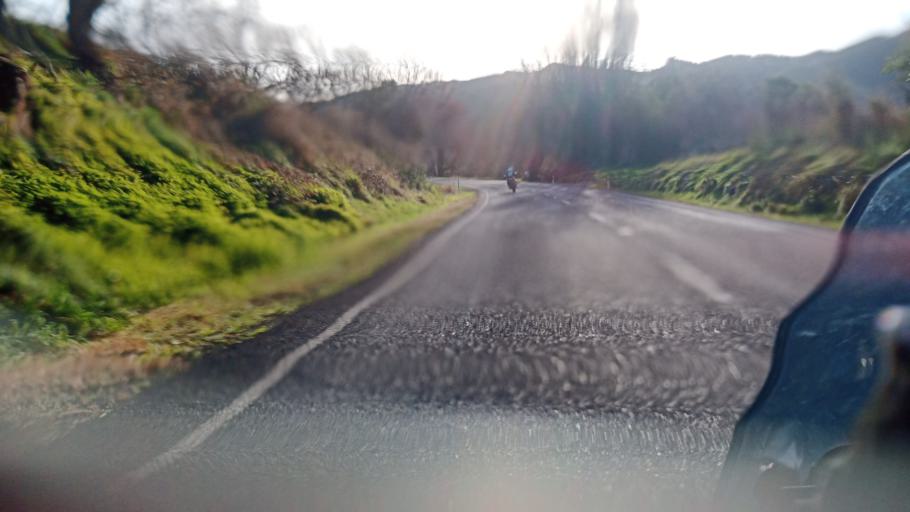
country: NZ
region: Gisborne
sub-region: Gisborne District
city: Gisborne
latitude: -38.4460
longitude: 177.6220
